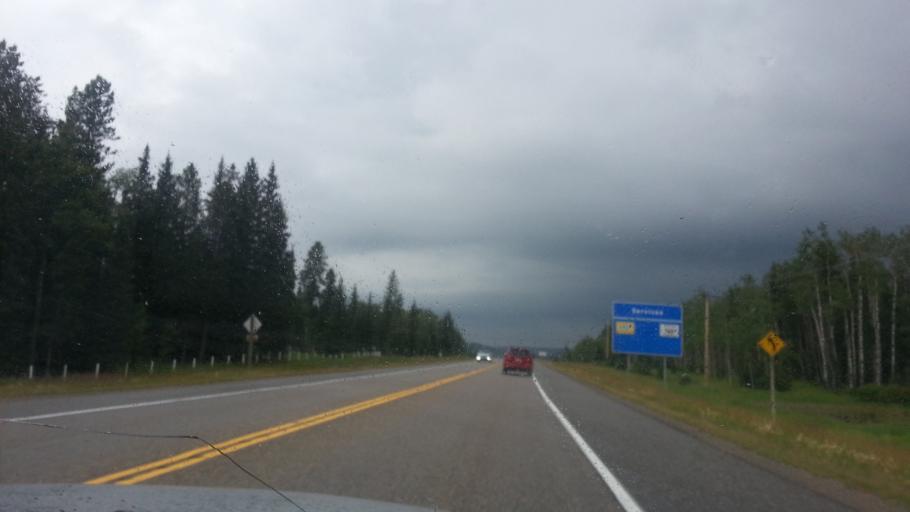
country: CA
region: Alberta
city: Cochrane
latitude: 50.9379
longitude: -114.5601
